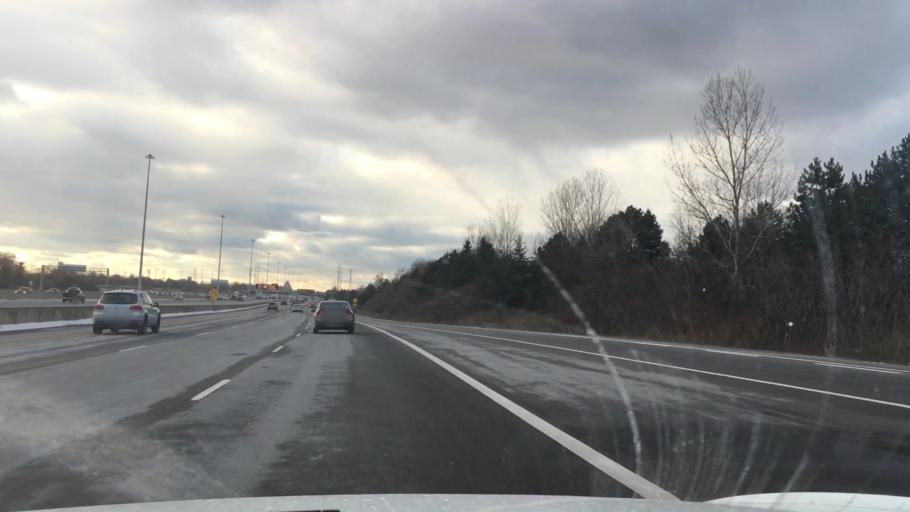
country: CA
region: Ontario
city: Scarborough
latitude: 43.8005
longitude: -79.1733
